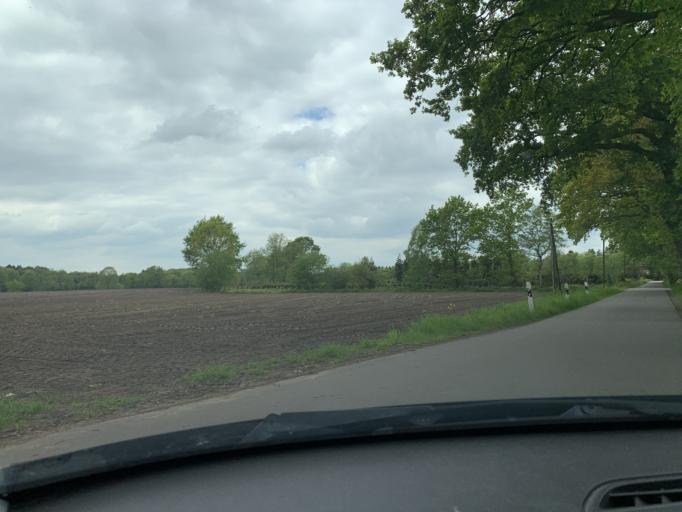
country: DE
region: Lower Saxony
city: Westerstede
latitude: 53.2420
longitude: 7.9198
